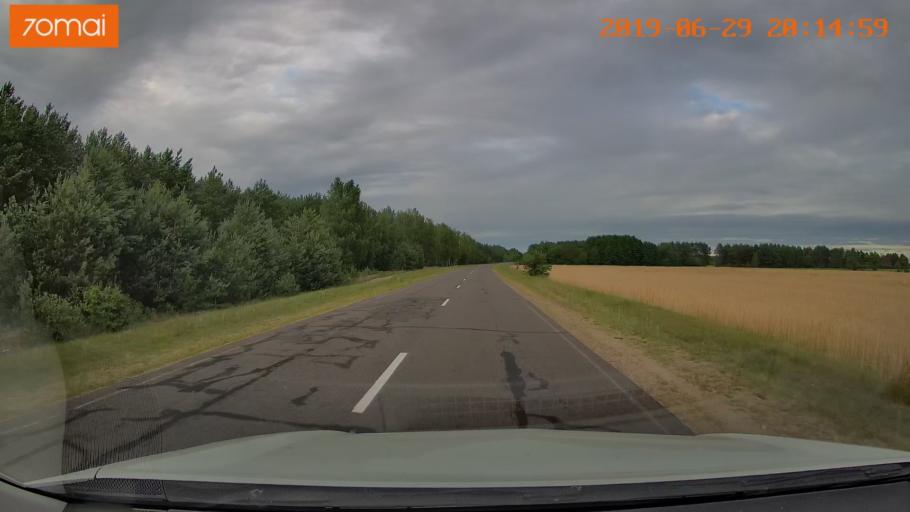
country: BY
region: Brest
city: Lahishyn
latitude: 52.3710
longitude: 26.1671
